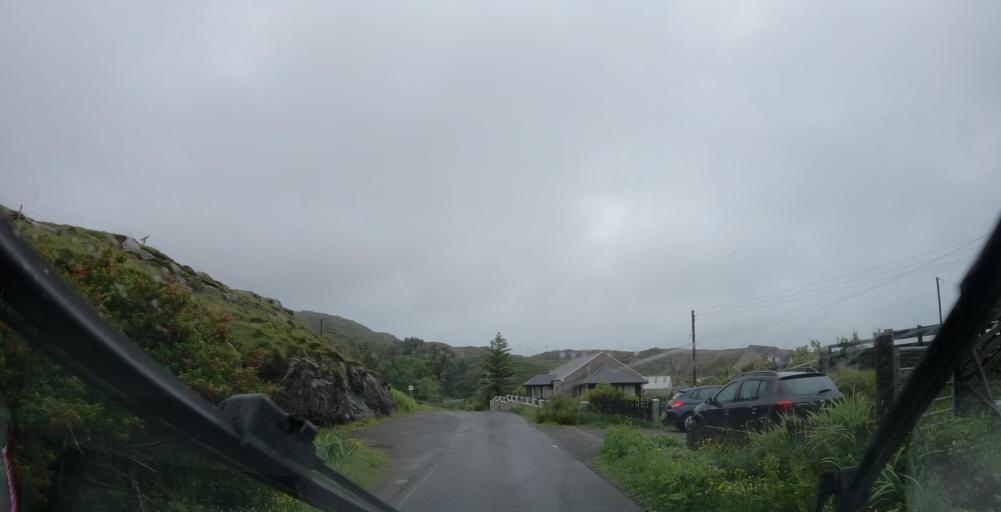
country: GB
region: Scotland
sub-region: Eilean Siar
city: Barra
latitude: 57.0107
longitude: -7.4313
